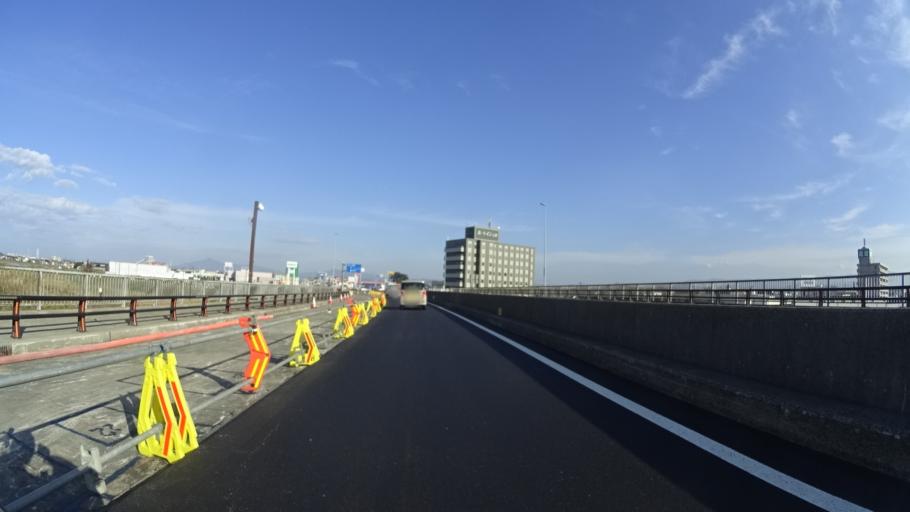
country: JP
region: Niigata
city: Joetsu
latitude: 37.1621
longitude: 138.2462
